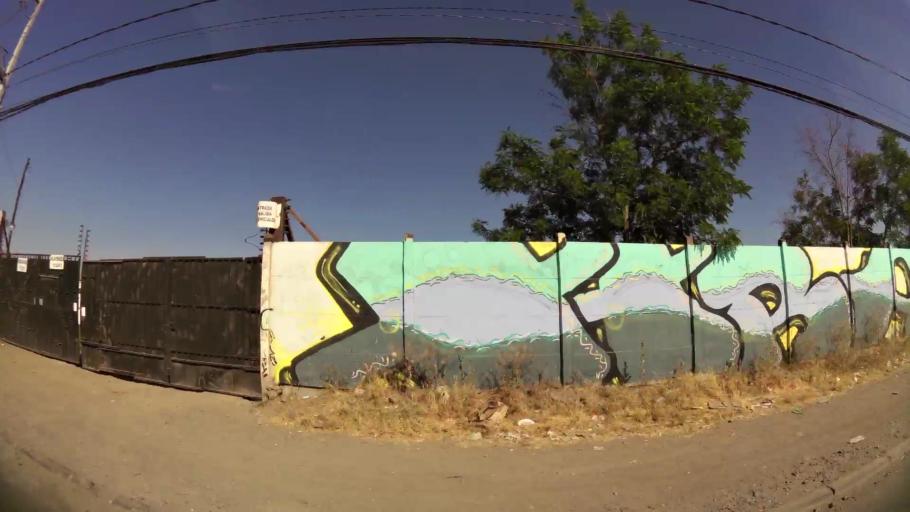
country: CL
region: Santiago Metropolitan
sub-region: Provincia de Maipo
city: San Bernardo
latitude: -33.5717
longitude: -70.7003
